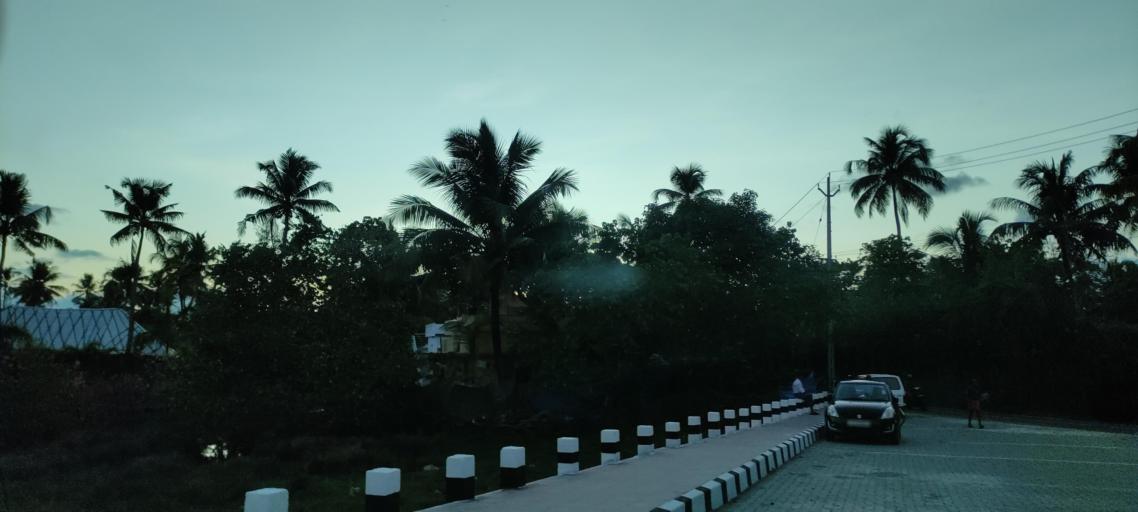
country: IN
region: Kerala
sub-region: Alappuzha
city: Kutiatodu
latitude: 9.7504
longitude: 76.2856
